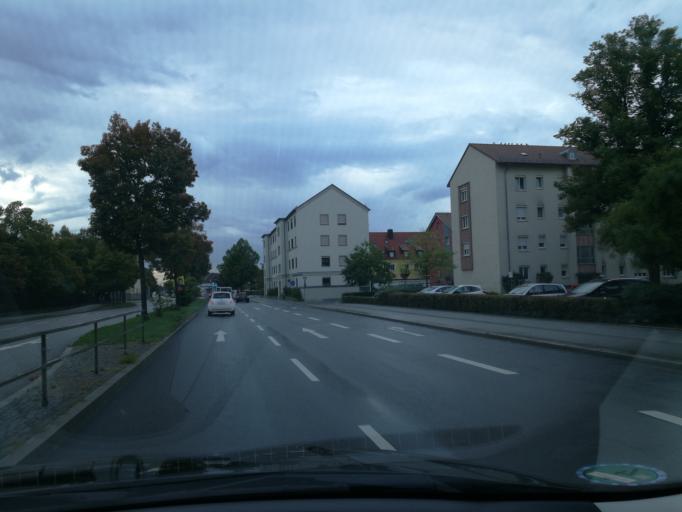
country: DE
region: Bavaria
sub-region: Upper Palatinate
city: Regensburg
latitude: 49.0050
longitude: 12.1199
